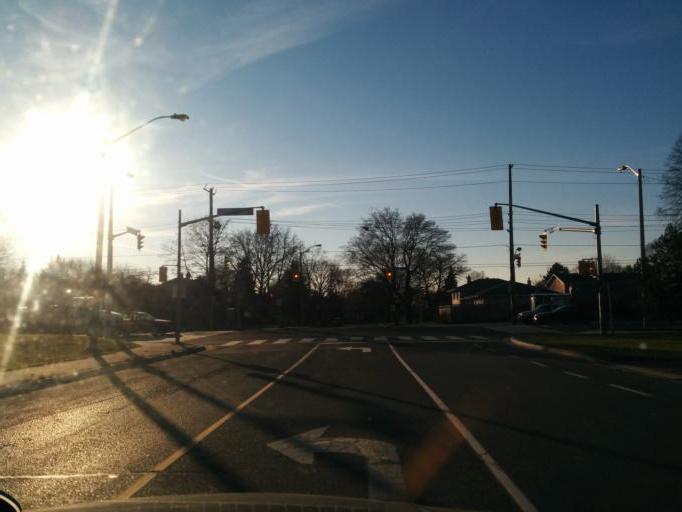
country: CA
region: Ontario
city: Etobicoke
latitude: 43.6737
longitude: -79.5487
